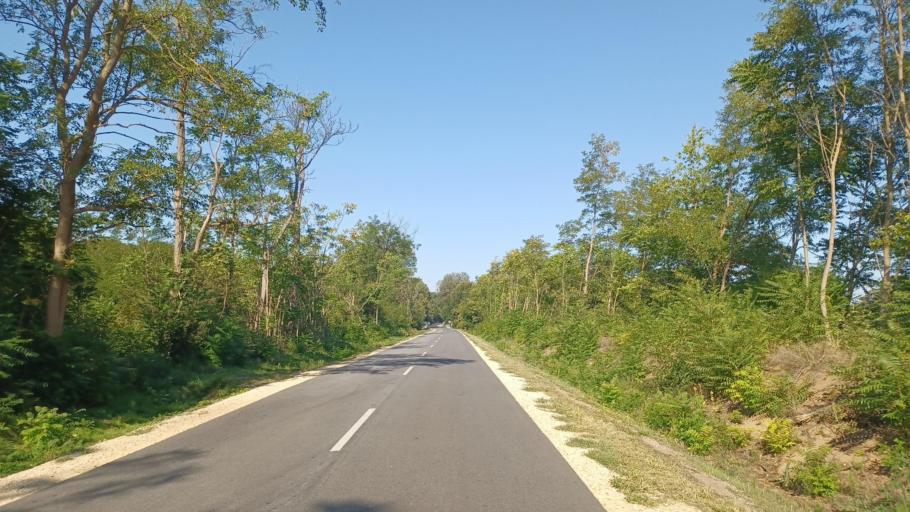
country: HU
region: Tolna
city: Nemetker
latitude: 46.7303
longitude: 18.7314
